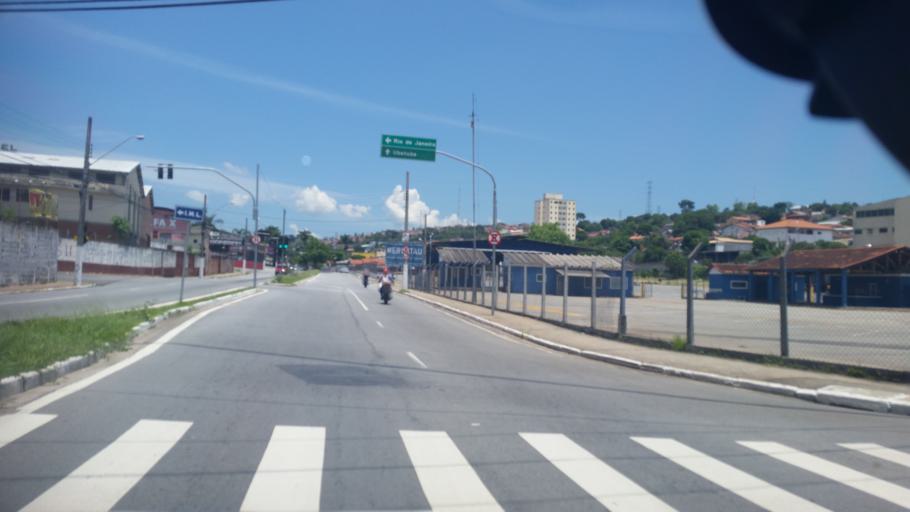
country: BR
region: Sao Paulo
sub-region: Taubate
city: Taubate
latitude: -23.0389
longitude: -45.5650
